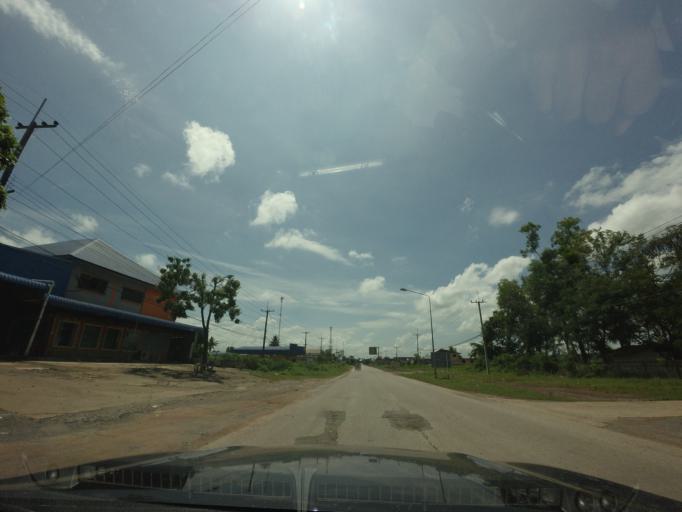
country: TH
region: Nong Khai
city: Pho Tak
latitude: 17.7750
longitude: 102.3954
